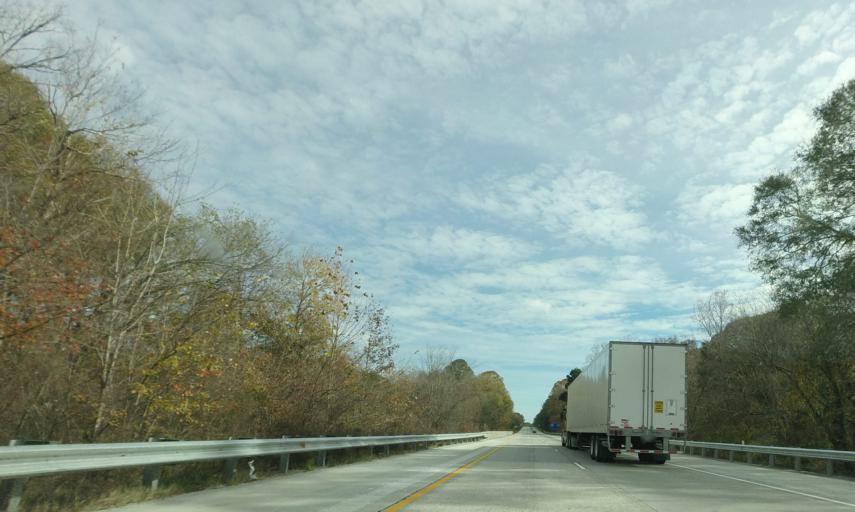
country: US
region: Georgia
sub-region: Laurens County
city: Dublin
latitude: 32.5031
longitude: -83.0099
